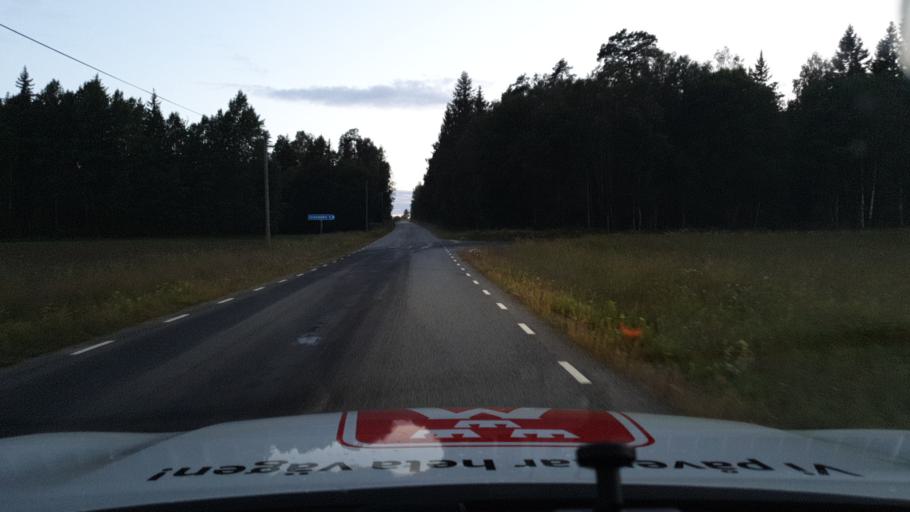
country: SE
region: Uppsala
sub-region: Heby Kommun
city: Heby
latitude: 59.9631
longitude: 16.8134
